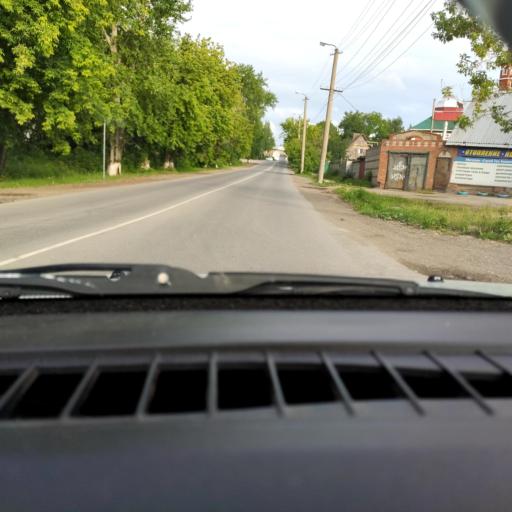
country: RU
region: Perm
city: Kungur
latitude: 57.4236
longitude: 56.9572
